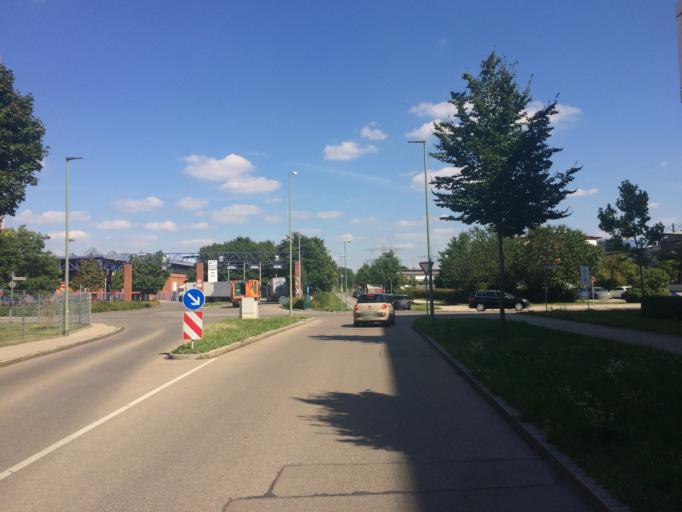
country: DE
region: Bavaria
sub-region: Swabia
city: Augsburg
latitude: 48.4007
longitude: 10.9316
